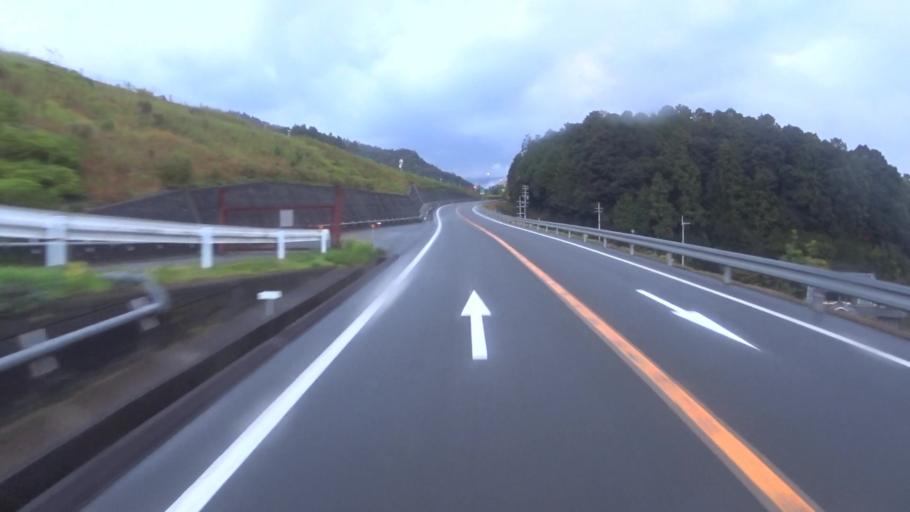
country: JP
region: Kyoto
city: Miyazu
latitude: 35.4304
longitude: 135.2099
